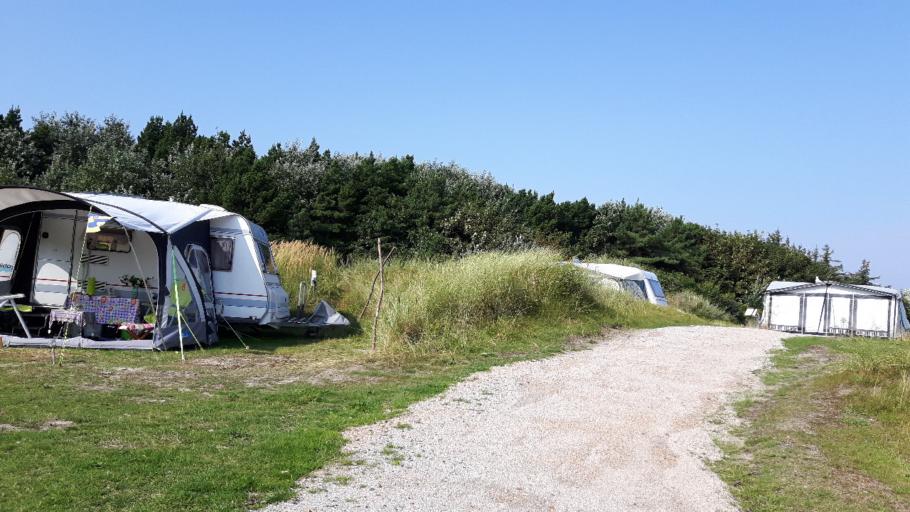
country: NL
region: Friesland
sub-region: Gemeente Ameland
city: Nes
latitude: 53.4573
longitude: 5.7661
